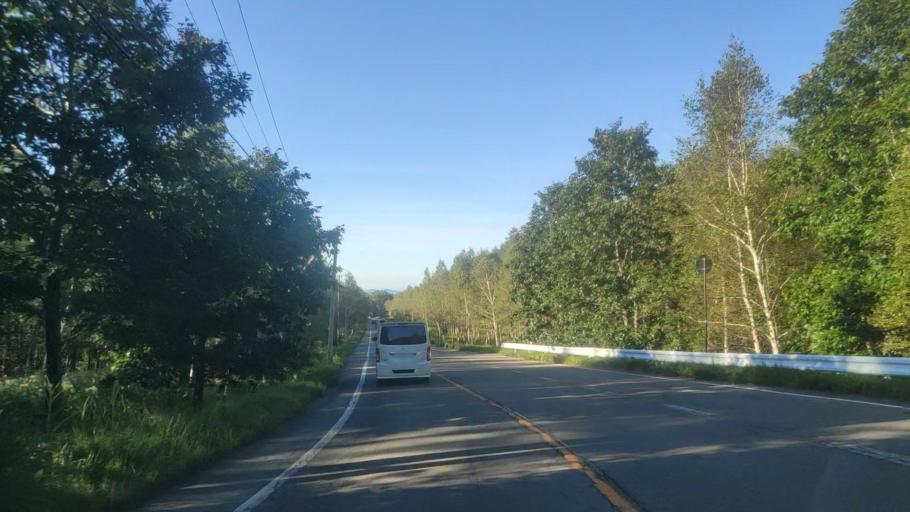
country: JP
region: Nagano
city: Kamimaruko
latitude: 36.1616
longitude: 138.2812
